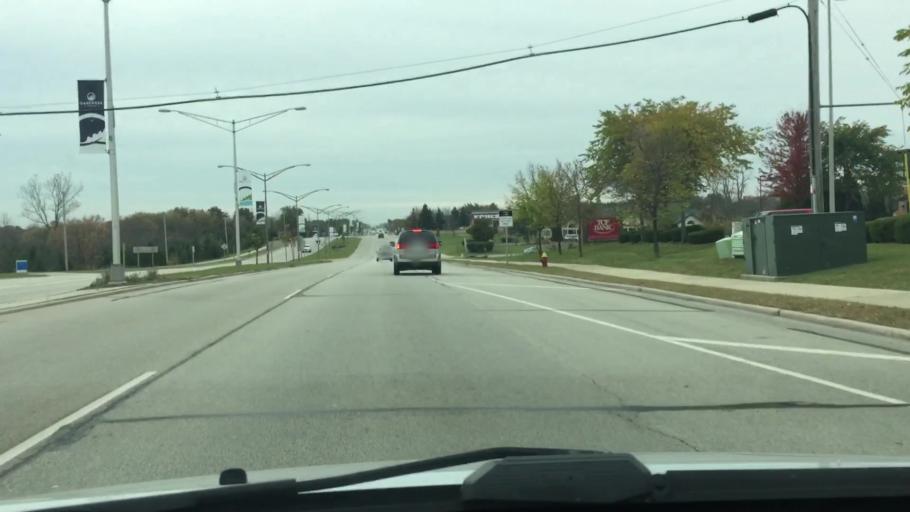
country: US
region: Wisconsin
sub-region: Milwaukee County
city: Oak Creek
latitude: 42.8823
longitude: -87.9125
